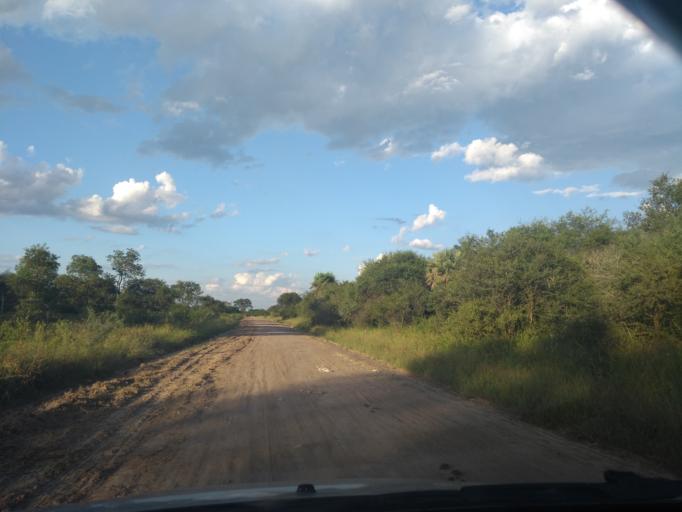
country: AR
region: Chaco
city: Colonia Benitez
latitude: -27.3871
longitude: -58.9437
